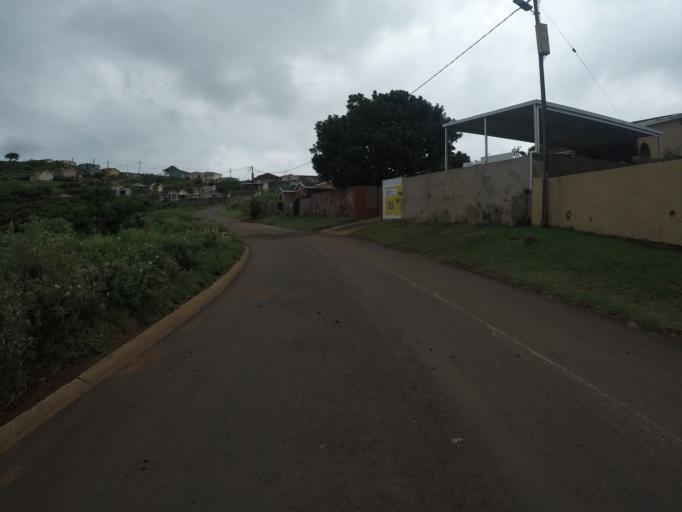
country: ZA
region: KwaZulu-Natal
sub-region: uThungulu District Municipality
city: Empangeni
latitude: -28.7703
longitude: 31.8615
